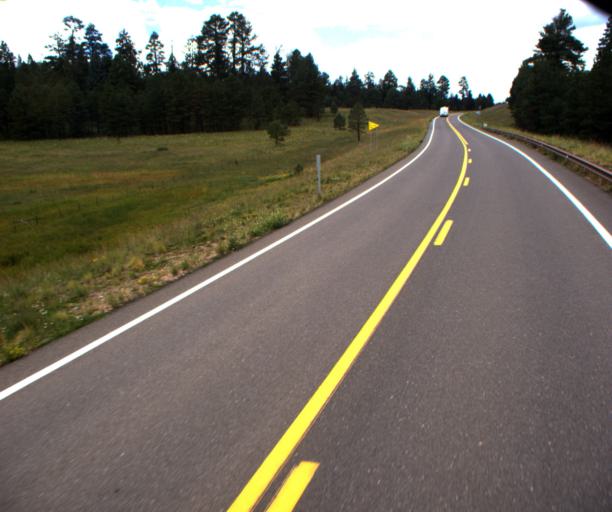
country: US
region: Arizona
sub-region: Apache County
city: Eagar
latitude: 33.9835
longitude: -109.5044
